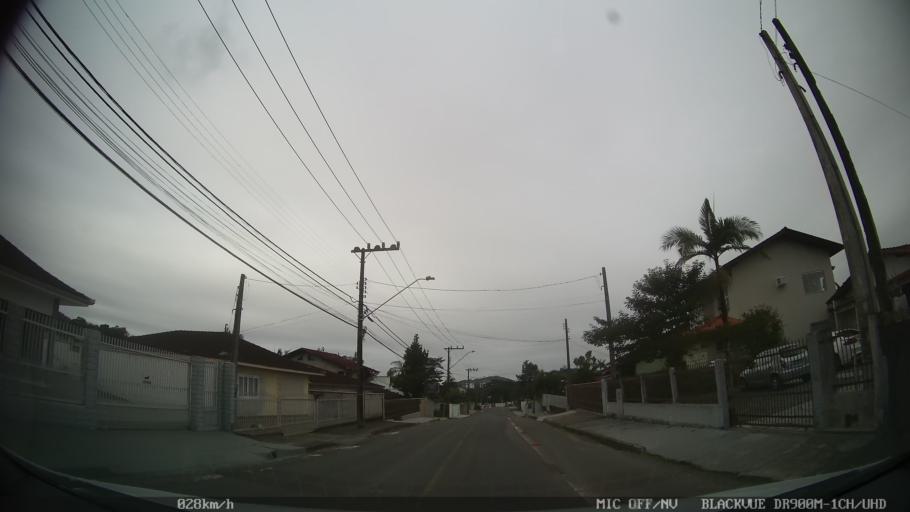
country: BR
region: Santa Catarina
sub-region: Joinville
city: Joinville
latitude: -26.2712
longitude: -48.8400
